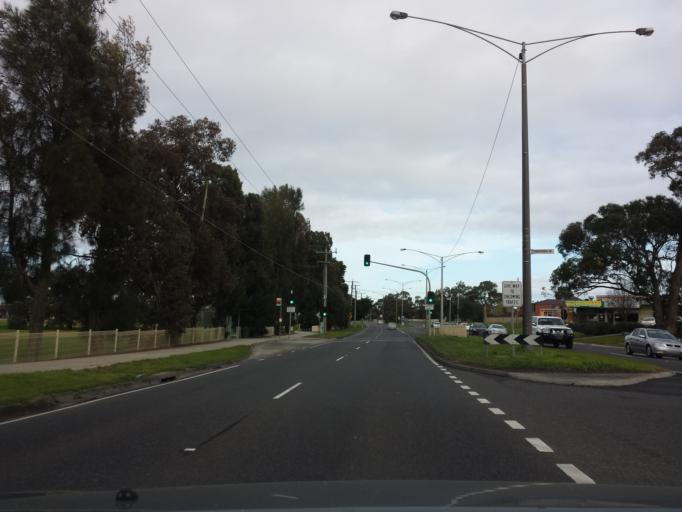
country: AU
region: Victoria
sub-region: Knox
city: Knoxfield
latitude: -37.8948
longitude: 145.2506
